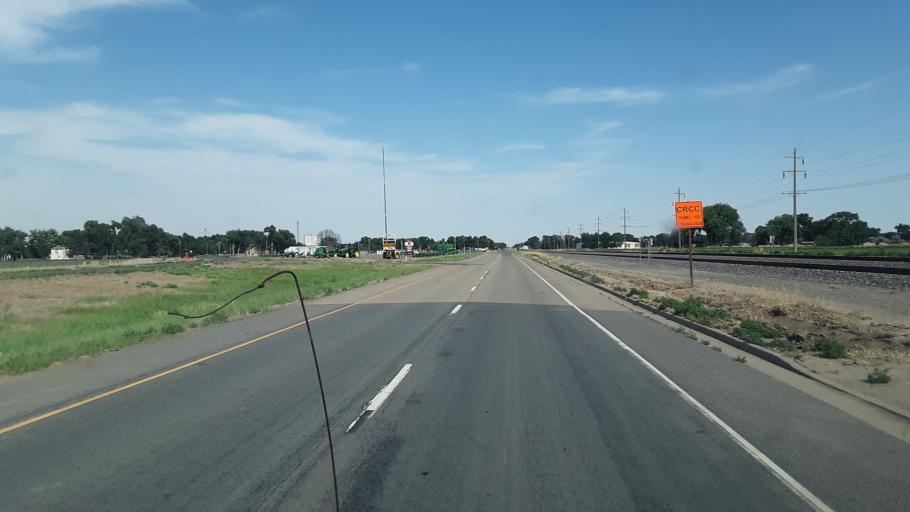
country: US
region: Colorado
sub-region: Otero County
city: Rocky Ford
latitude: 38.0627
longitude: -103.7441
